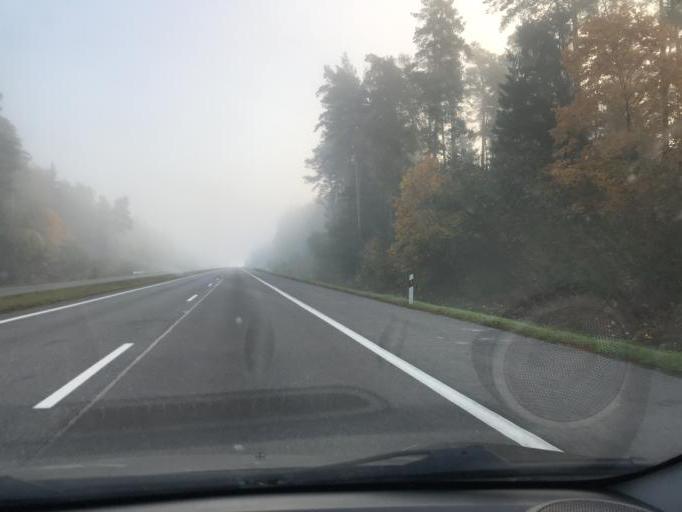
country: BY
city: Michanovichi
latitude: 53.7680
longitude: 27.6826
